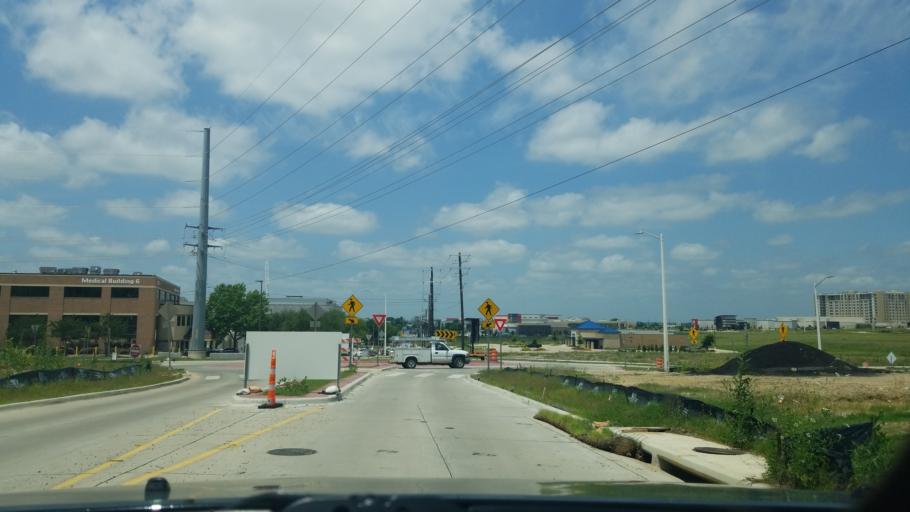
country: US
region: Texas
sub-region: Denton County
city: Denton
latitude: 33.2190
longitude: -97.1612
